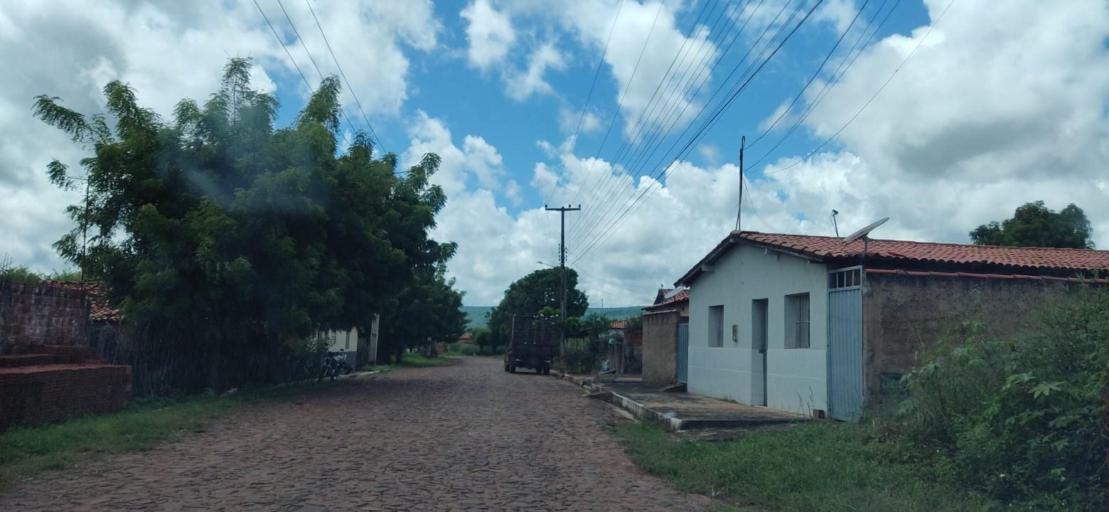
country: BR
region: Piaui
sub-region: Valenca Do Piaui
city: Valenca do Piaui
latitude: -6.1113
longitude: -41.7985
